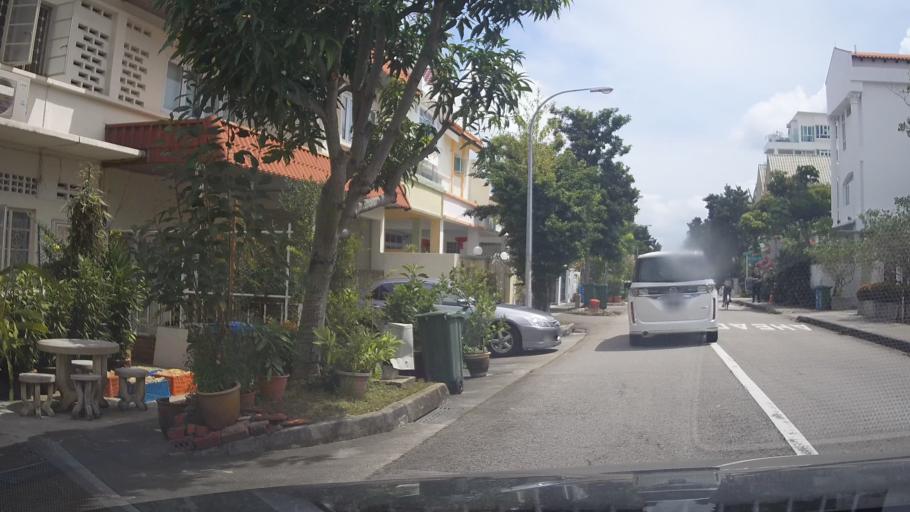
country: SG
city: Singapore
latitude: 1.3147
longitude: 103.9023
